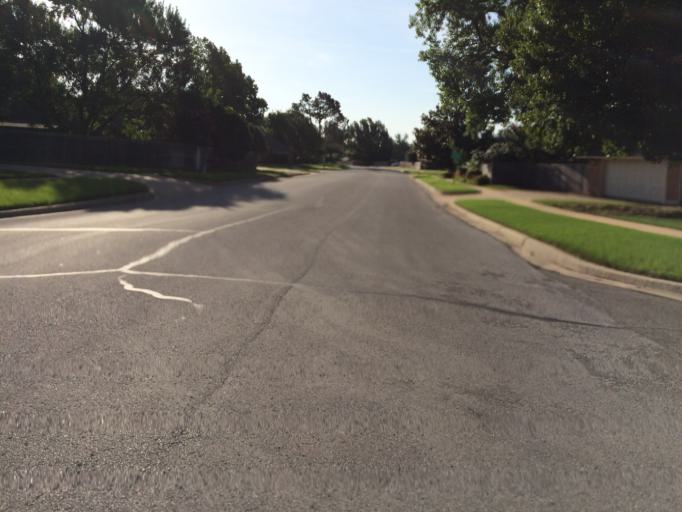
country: US
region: Oklahoma
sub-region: Cleveland County
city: Norman
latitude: 35.2239
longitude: -97.5011
